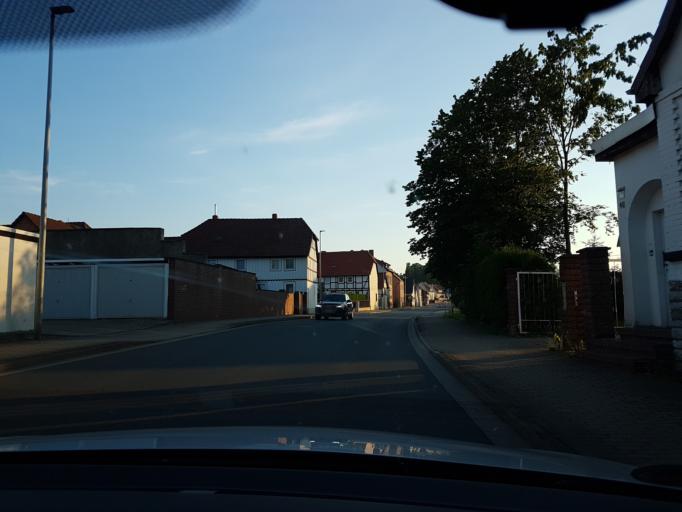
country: DE
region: Lower Saxony
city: Schoningen
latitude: 52.1592
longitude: 10.9643
